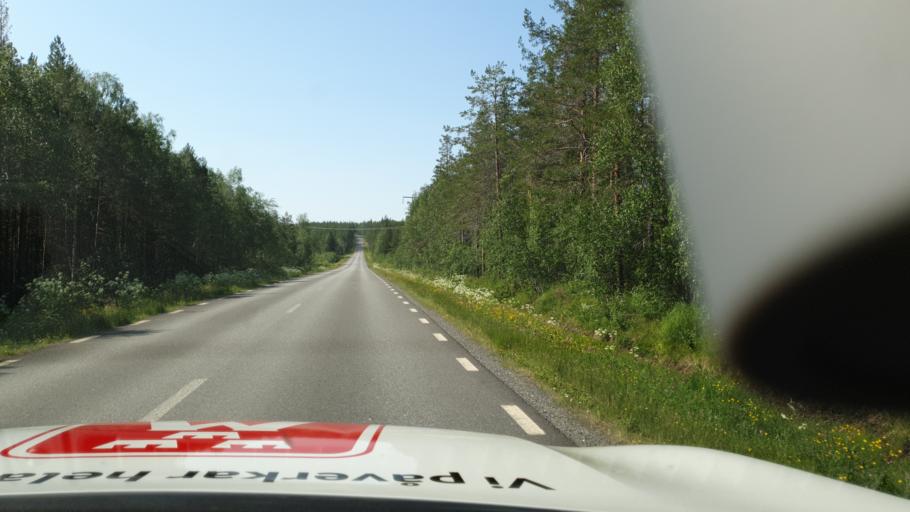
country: SE
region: Vaesterbotten
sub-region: Skelleftea Kommun
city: Langsele
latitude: 64.9816
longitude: 20.0668
